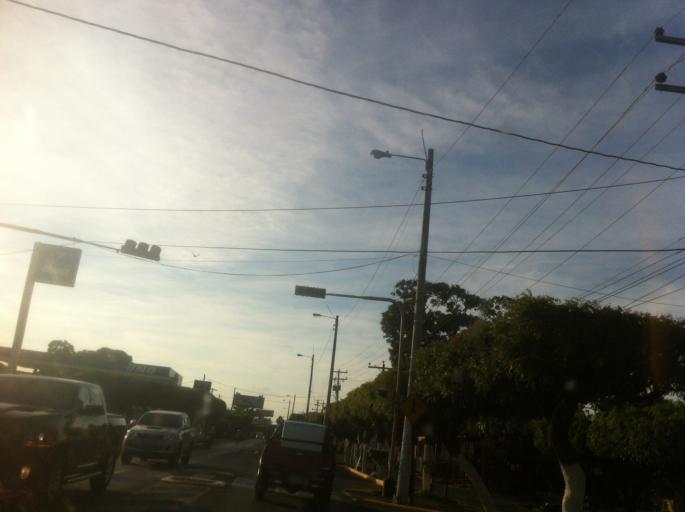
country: NI
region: Rivas
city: Rivas
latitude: 11.4245
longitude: -85.8041
